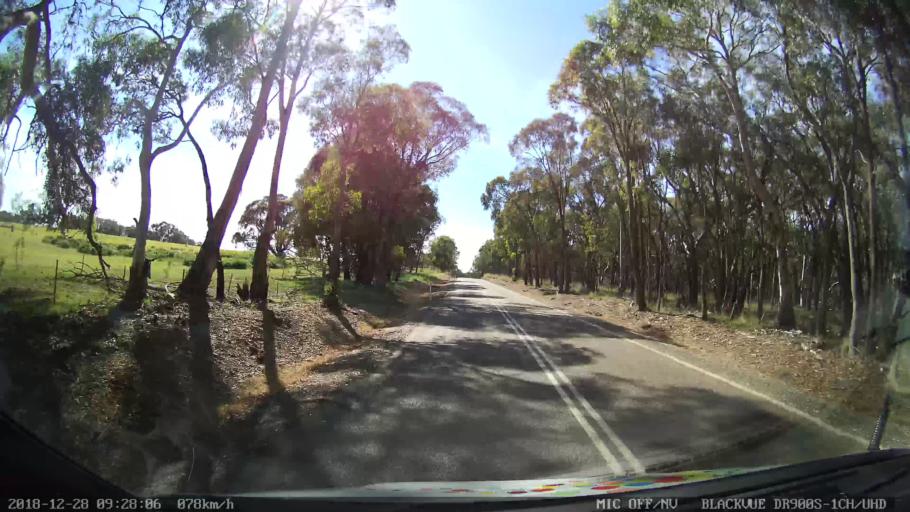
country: AU
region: New South Wales
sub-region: Upper Lachlan Shire
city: Crookwell
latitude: -34.4365
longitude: 149.4120
